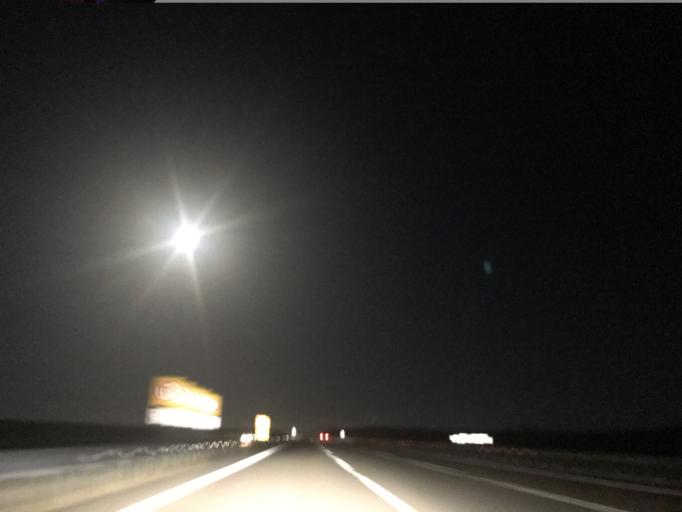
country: TR
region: Nigde
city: Ulukisla
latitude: 37.6377
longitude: 34.3984
